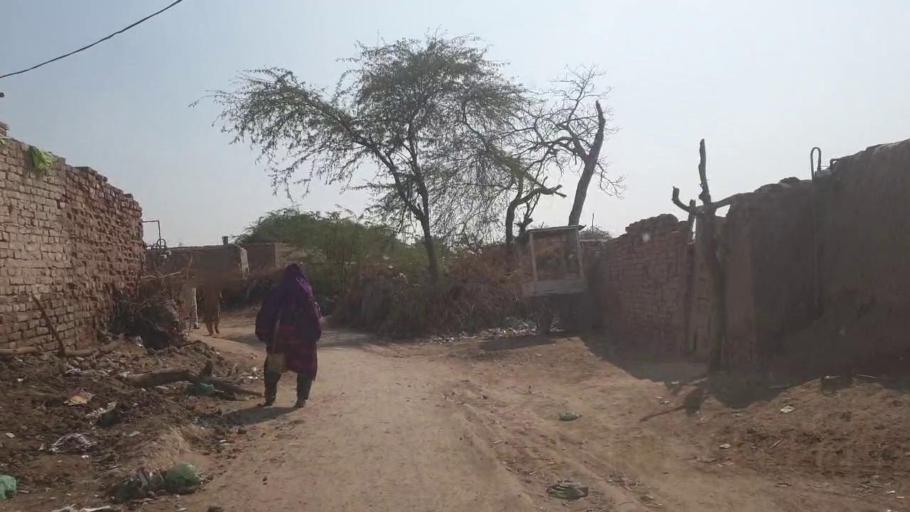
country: PK
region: Sindh
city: Mirpur Khas
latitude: 25.4912
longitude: 68.8870
